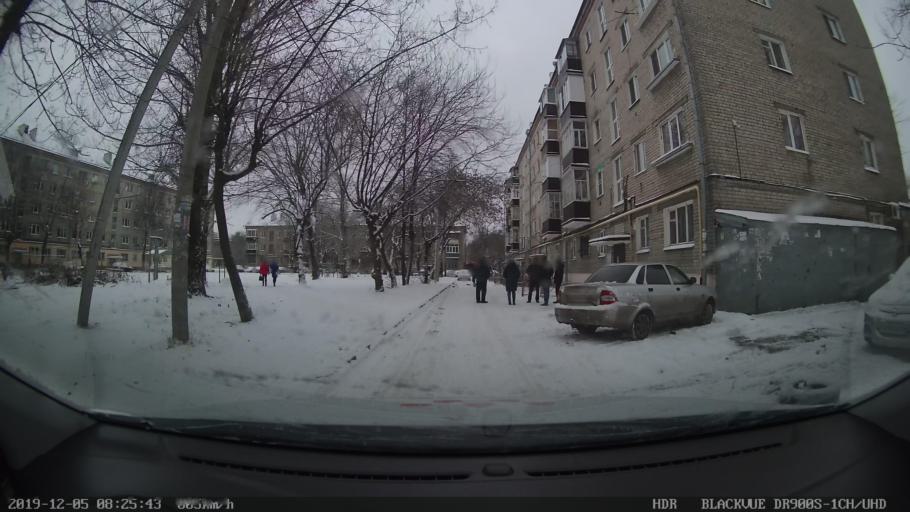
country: RU
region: Tatarstan
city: Staroye Arakchino
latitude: 55.8748
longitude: 49.0214
